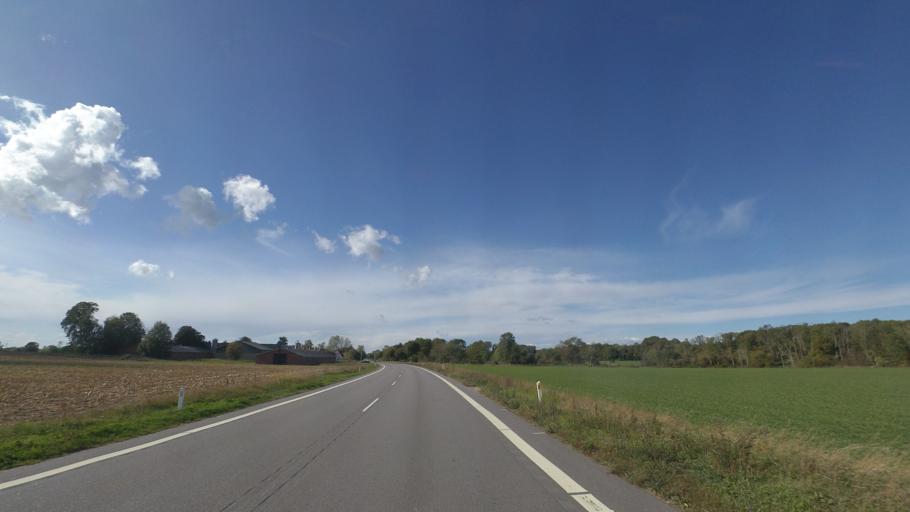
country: DK
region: Capital Region
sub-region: Bornholm Kommune
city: Ronne
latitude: 55.0741
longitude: 14.7952
